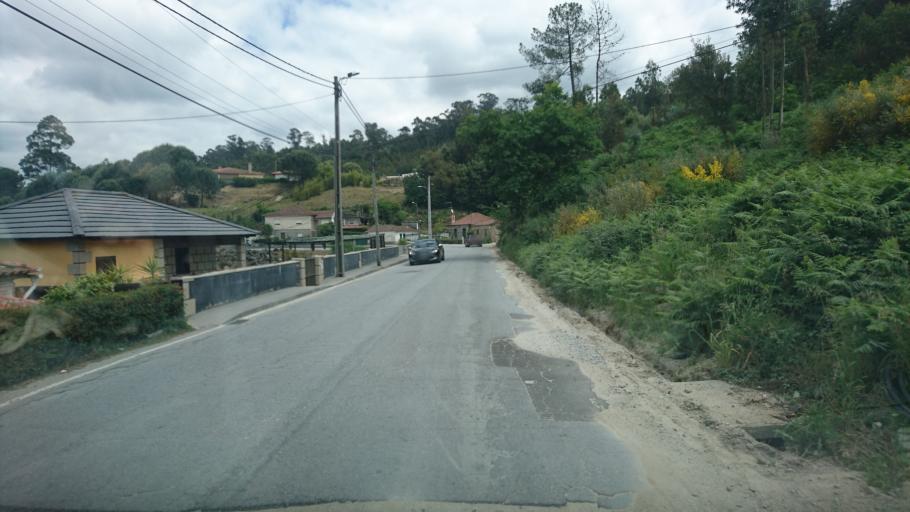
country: PT
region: Porto
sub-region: Paredes
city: Baltar
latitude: 41.1596
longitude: -8.3588
